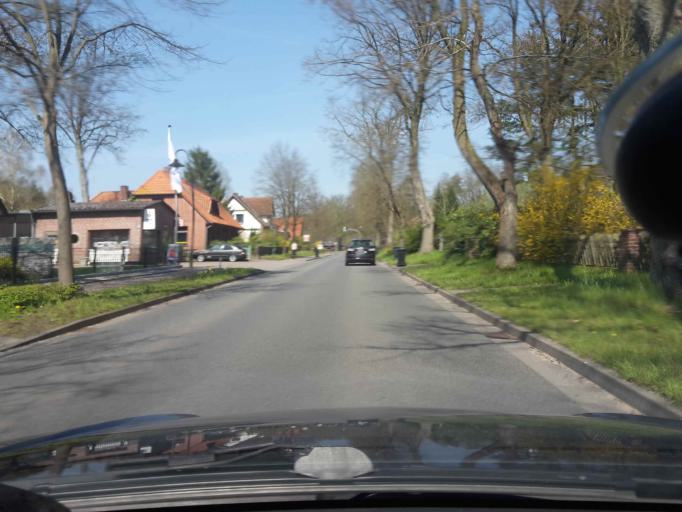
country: DE
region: Lower Saxony
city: Handeloh
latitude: 53.2445
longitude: 9.8422
